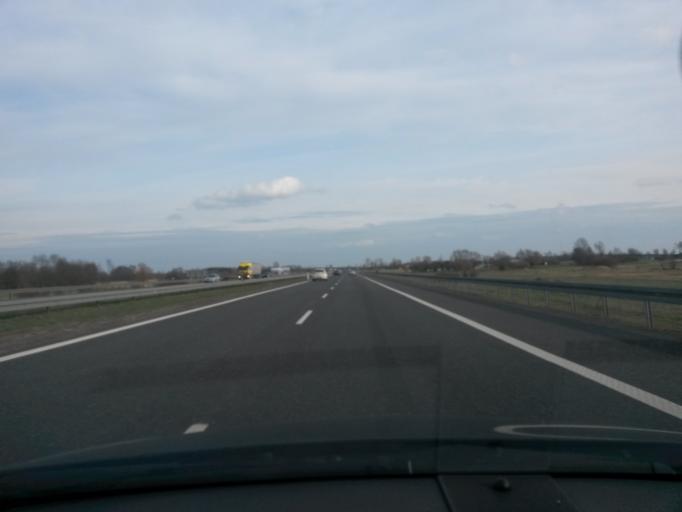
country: PL
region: Greater Poland Voivodeship
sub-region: Powiat kolski
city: Dabie
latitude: 52.0565
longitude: 18.8391
